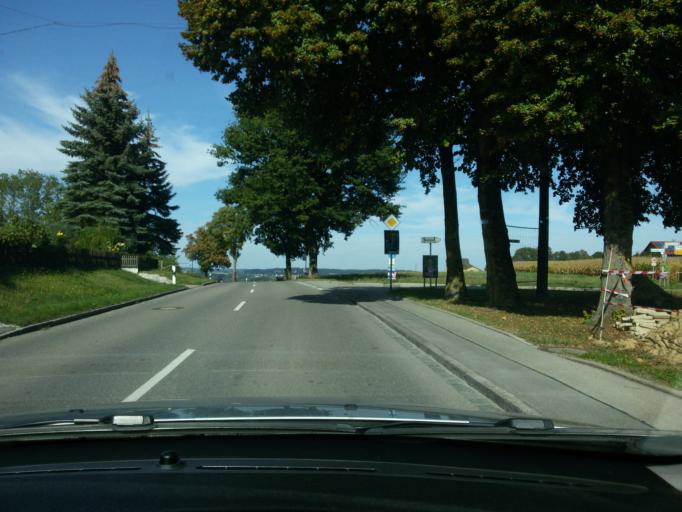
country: DE
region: Bavaria
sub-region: Swabia
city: Ustersbach
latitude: 48.3108
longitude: 10.6546
